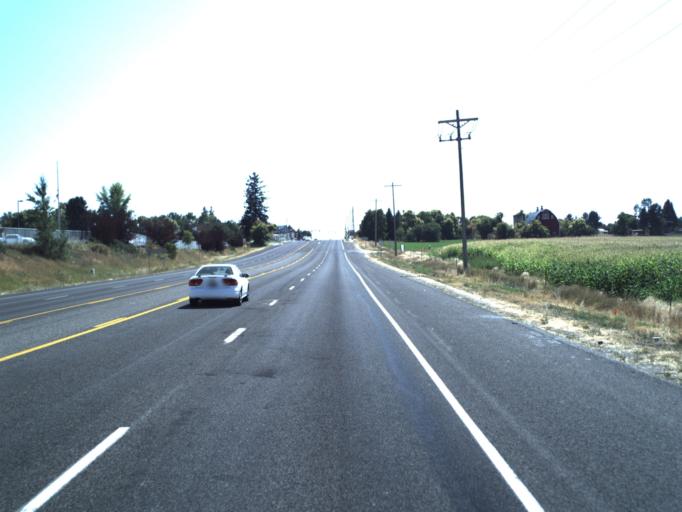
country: US
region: Utah
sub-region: Cache County
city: Richmond
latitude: 41.9277
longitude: -111.8143
